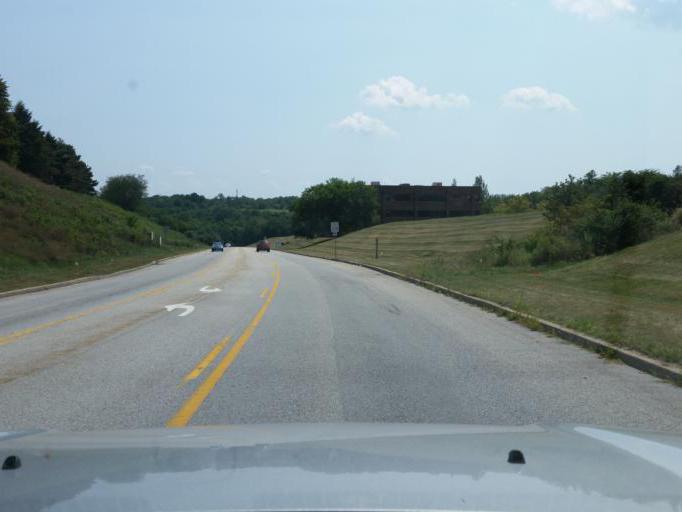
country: US
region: Pennsylvania
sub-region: Dauphin County
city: Lawnton
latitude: 40.2725
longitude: -76.8141
